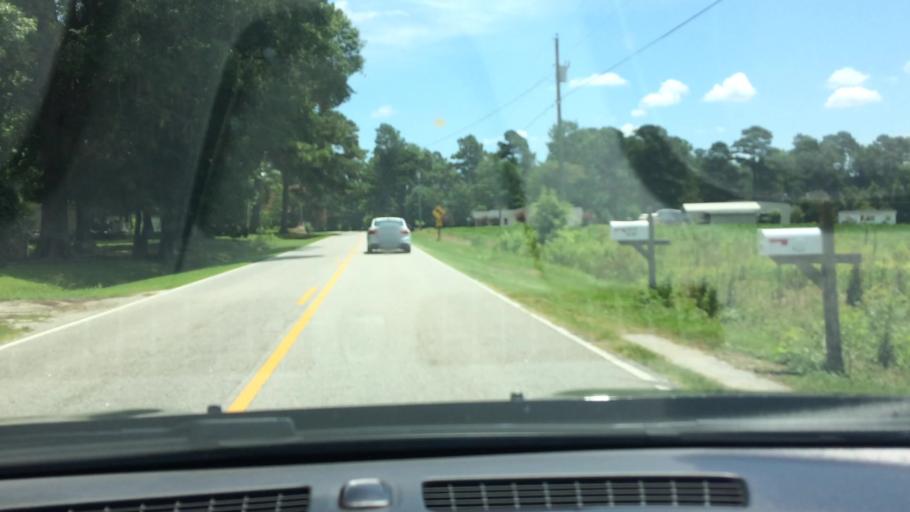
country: US
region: North Carolina
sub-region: Pitt County
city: Windsor
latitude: 35.5665
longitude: -77.2117
